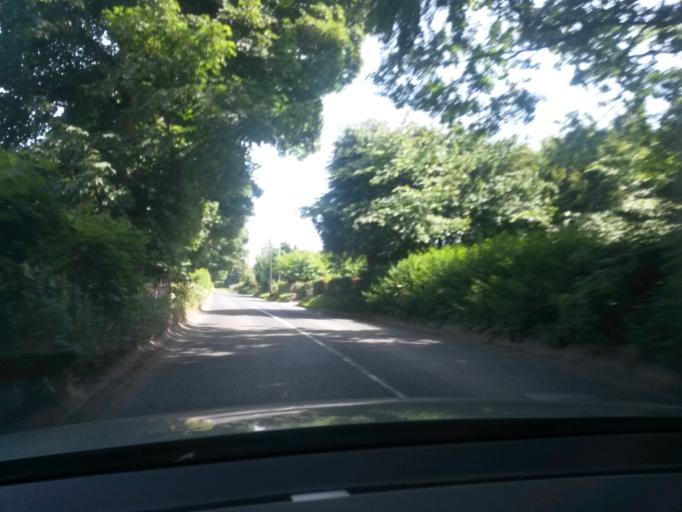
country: IE
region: Leinster
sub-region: Wicklow
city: Blessington
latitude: 53.1757
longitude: -6.5580
